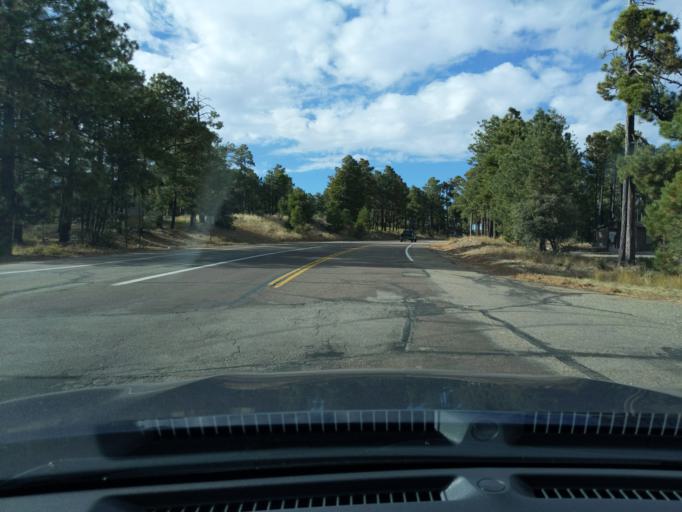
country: US
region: Arizona
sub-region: Pinal County
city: Oracle
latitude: 32.4331
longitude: -110.7509
